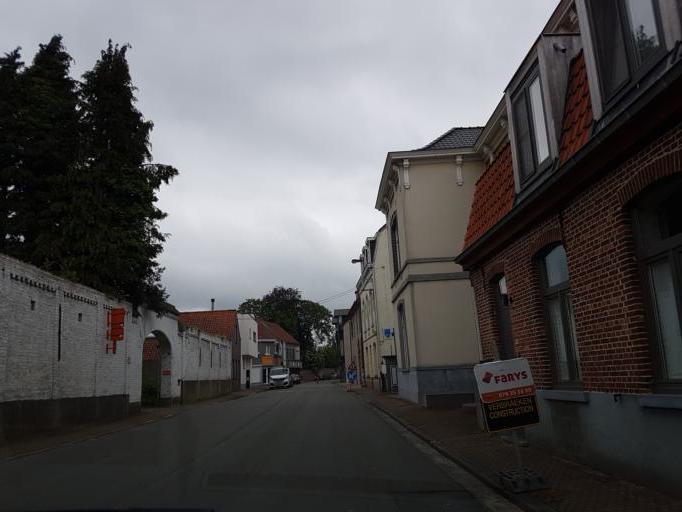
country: BE
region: Flanders
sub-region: Provincie Oost-Vlaanderen
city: Zomergem
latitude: 51.1156
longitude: 3.5613
